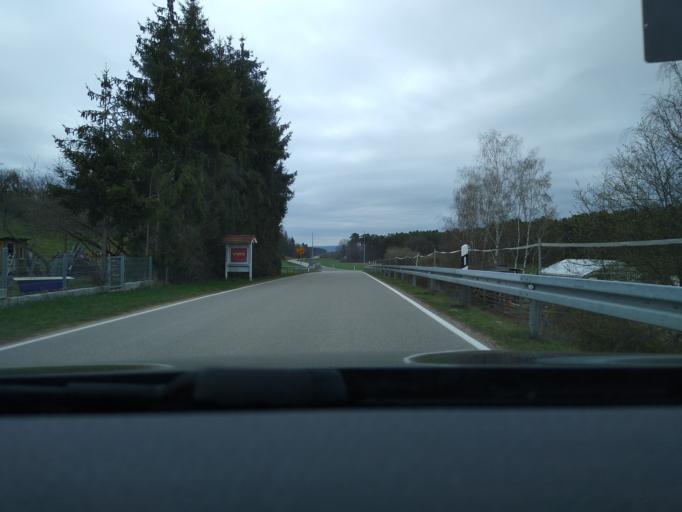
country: DE
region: Bavaria
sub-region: Regierungsbezirk Mittelfranken
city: Mohrendorf
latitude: 49.6546
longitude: 11.0085
